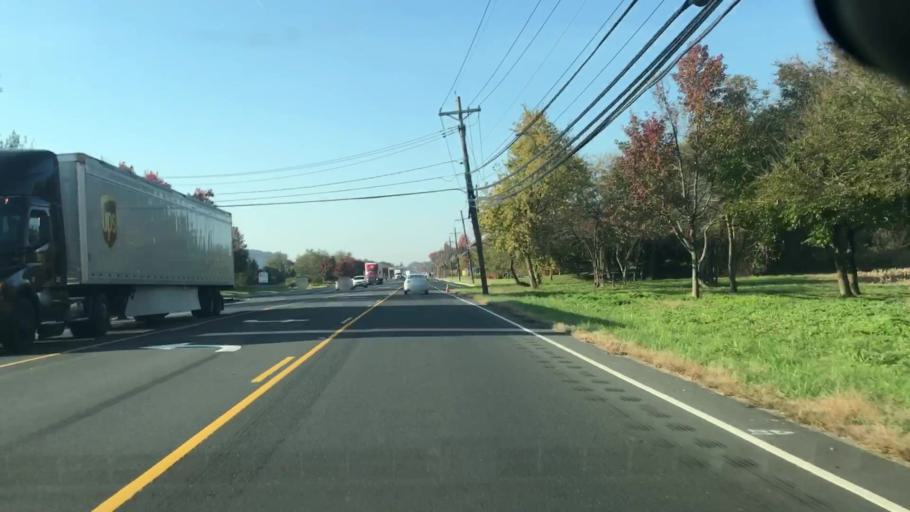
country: US
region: New Jersey
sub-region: Middlesex County
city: Rossmoor
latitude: 40.3328
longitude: -74.4911
